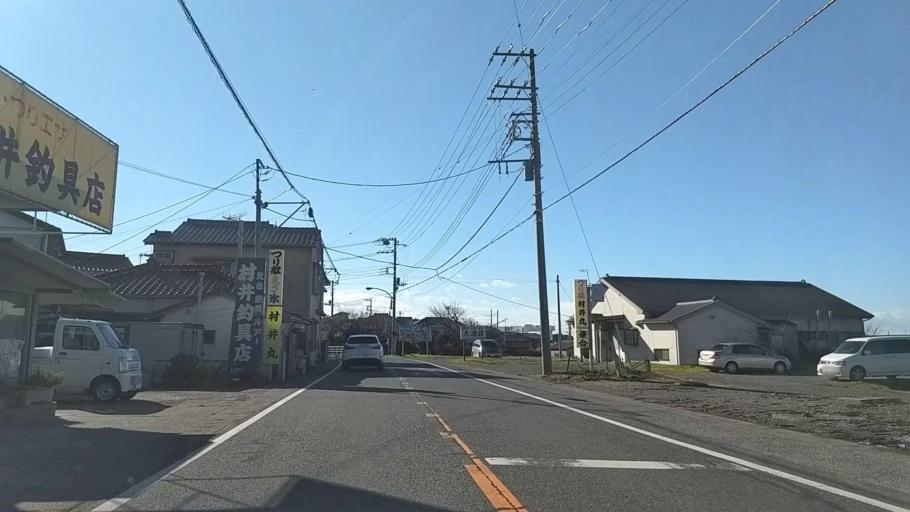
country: JP
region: Chiba
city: Tateyama
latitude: 35.1359
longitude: 139.8381
